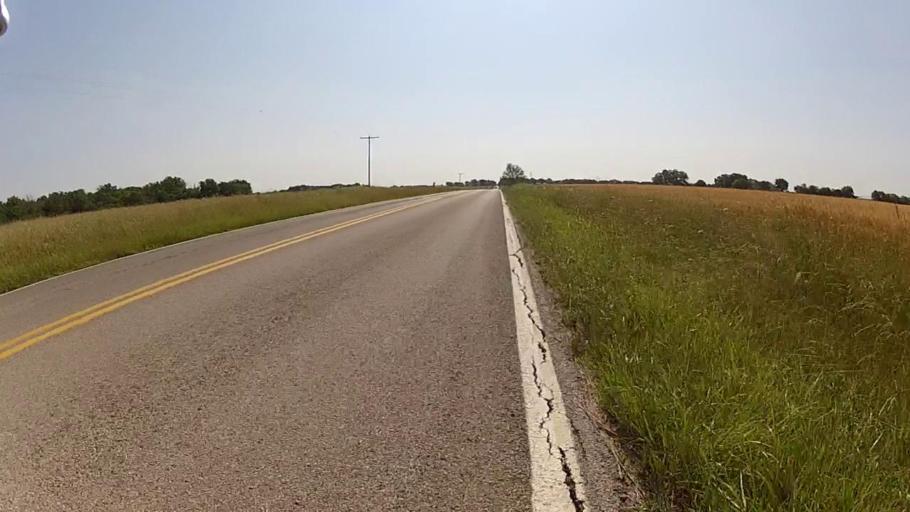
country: US
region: Kansas
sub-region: Montgomery County
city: Independence
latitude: 37.1930
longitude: -95.7524
